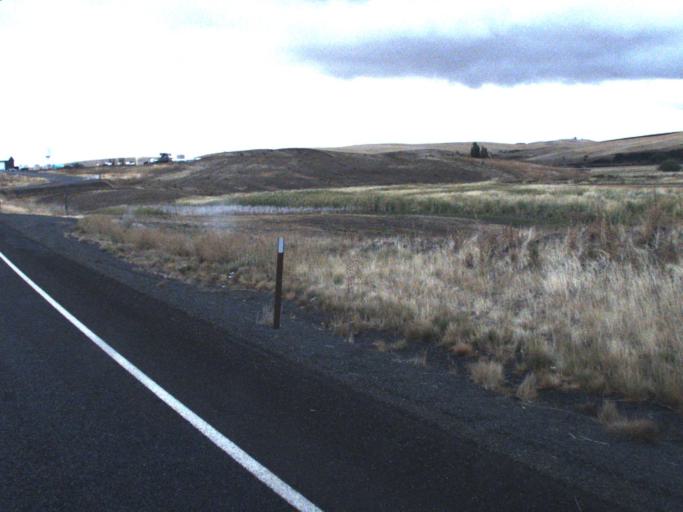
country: US
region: Washington
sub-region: Whitman County
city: Colfax
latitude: 47.2060
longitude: -117.3569
